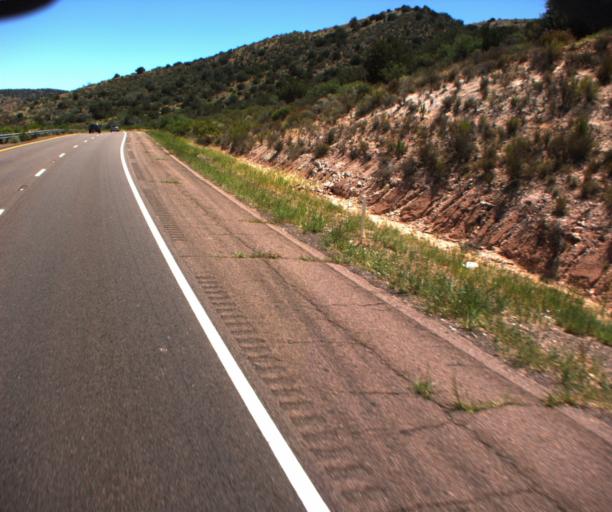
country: US
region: Arizona
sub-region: Gila County
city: Tonto Basin
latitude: 34.0215
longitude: -111.3610
